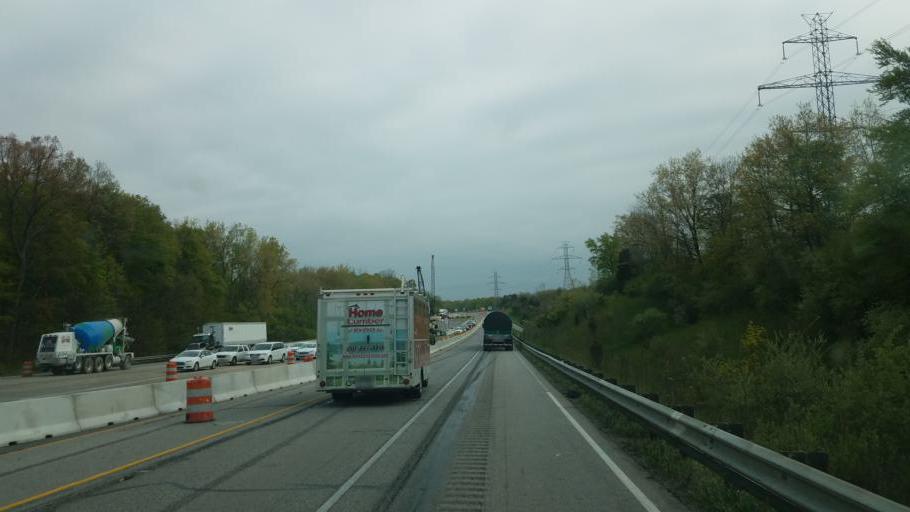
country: US
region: Indiana
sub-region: Allen County
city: Huntertown
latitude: 41.2289
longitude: -85.0993
